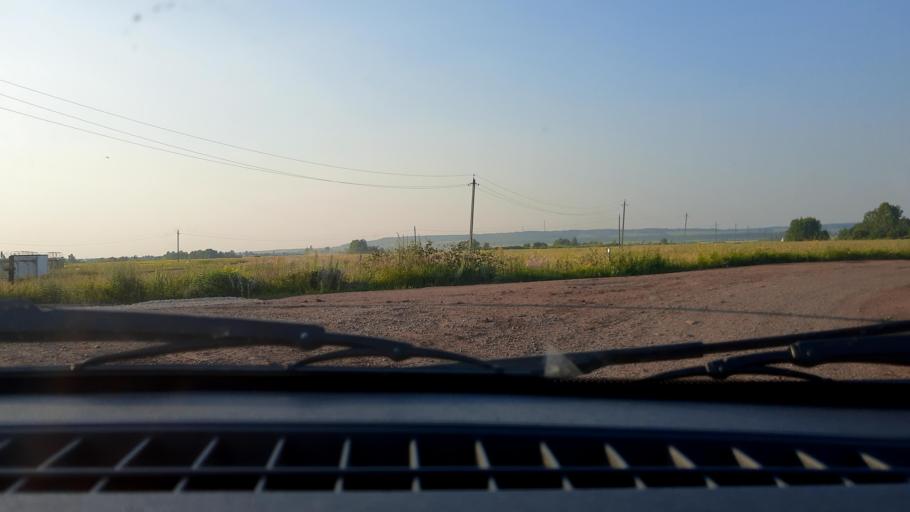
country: RU
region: Bashkortostan
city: Asanovo
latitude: 54.9336
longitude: 55.6242
